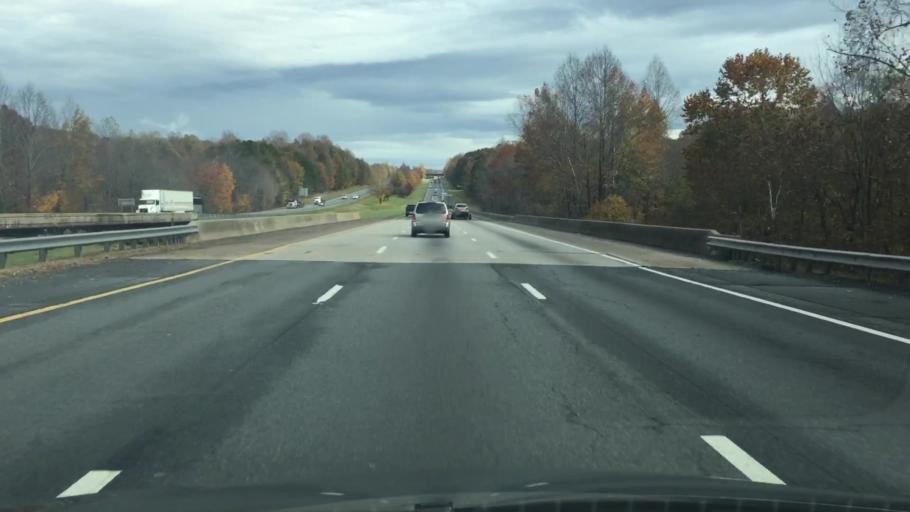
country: US
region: North Carolina
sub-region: Davidson County
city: Lexington
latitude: 35.7767
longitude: -80.2957
